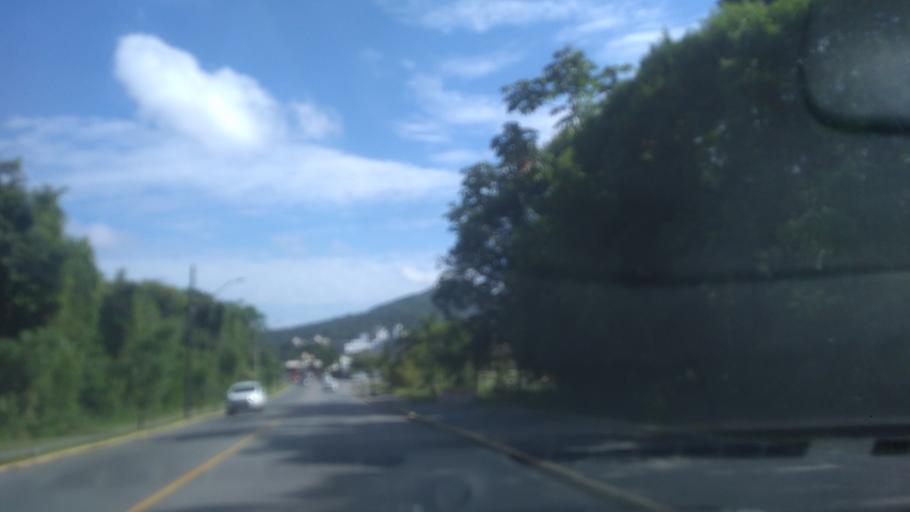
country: BR
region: Santa Catarina
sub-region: Joinville
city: Joinville
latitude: -26.3128
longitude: -48.8284
